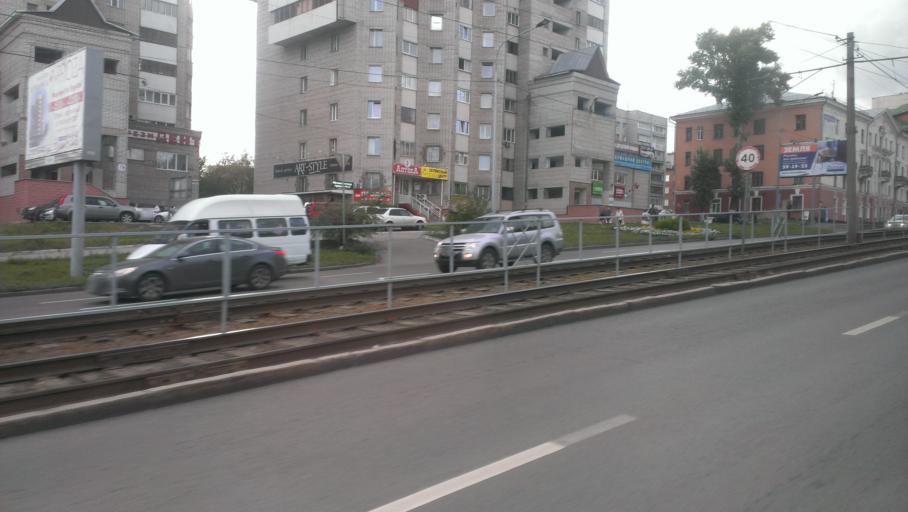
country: RU
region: Altai Krai
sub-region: Gorod Barnaulskiy
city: Barnaul
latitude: 53.3414
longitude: 83.7705
